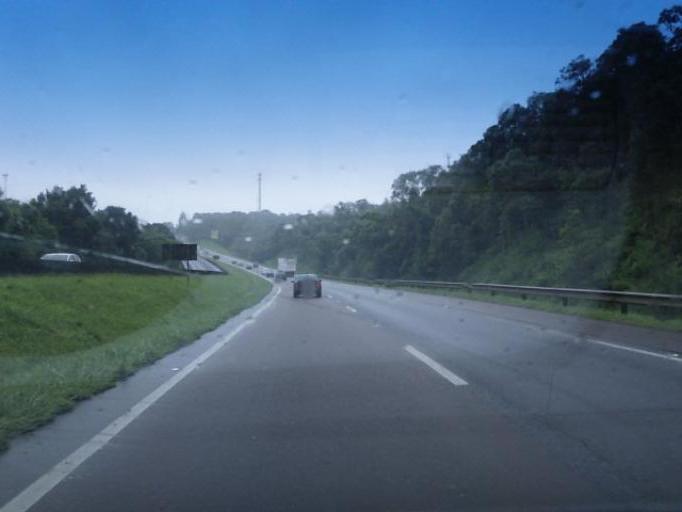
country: BR
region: Parana
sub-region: Sao Jose Dos Pinhais
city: Sao Jose dos Pinhais
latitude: -25.7848
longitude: -49.1216
